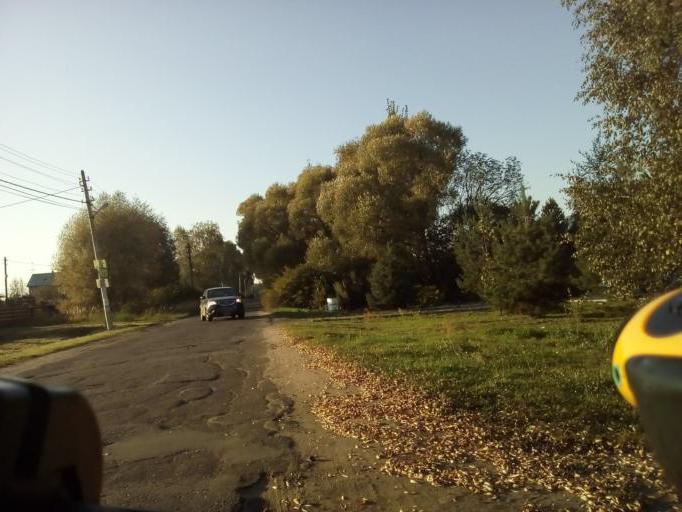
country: RU
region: Moskovskaya
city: Ramenskoye
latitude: 55.6086
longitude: 38.3006
